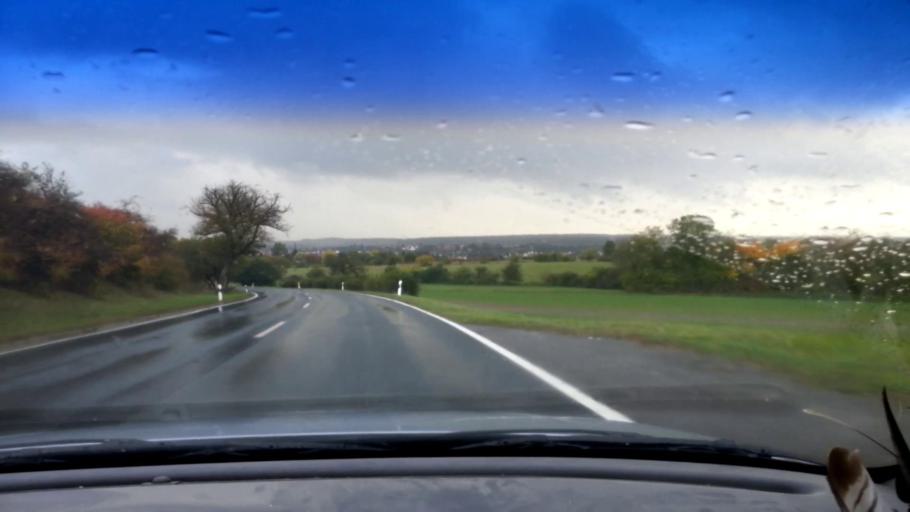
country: DE
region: Bavaria
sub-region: Upper Franconia
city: Burgebrach
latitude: 49.8389
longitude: 10.7346
